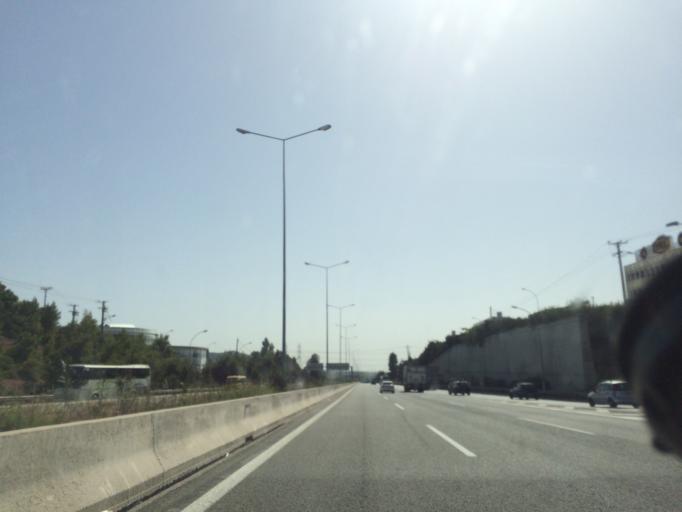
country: GR
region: Attica
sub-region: Nomarchia Anatolikis Attikis
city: Kryoneri
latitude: 38.1386
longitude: 23.8427
